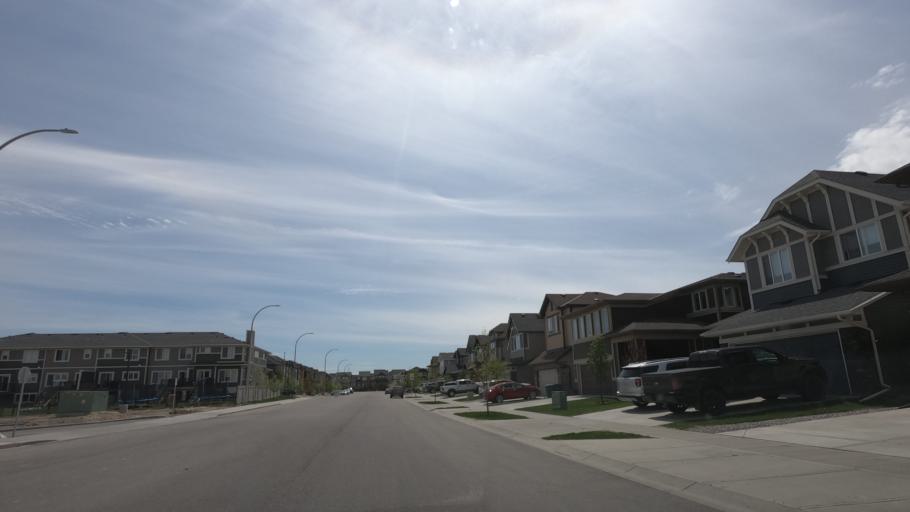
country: CA
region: Alberta
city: Airdrie
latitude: 51.2530
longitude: -114.0154
